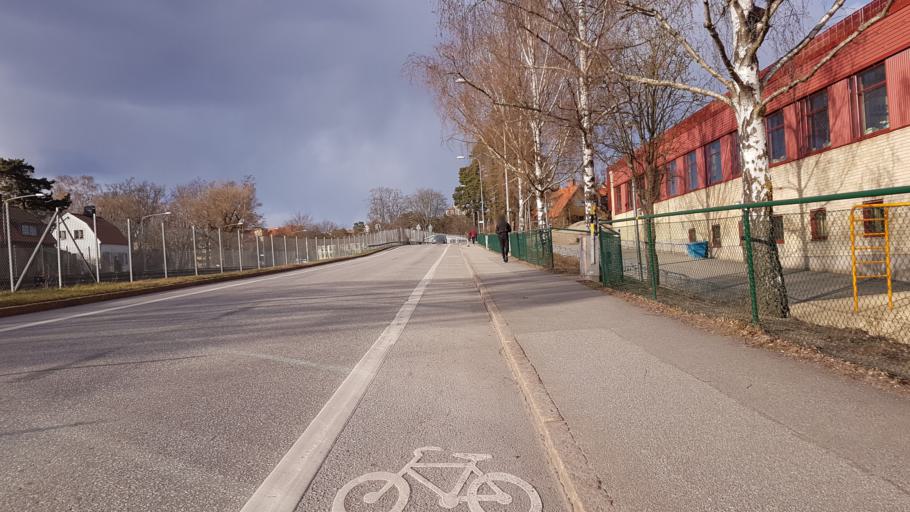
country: SE
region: Stockholm
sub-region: Stockholms Kommun
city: Arsta
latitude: 59.2913
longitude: 18.0704
